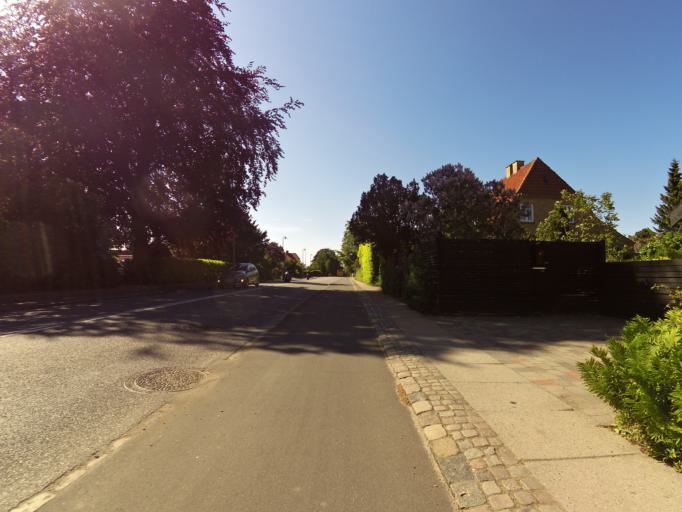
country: DK
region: Capital Region
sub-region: Gladsaxe Municipality
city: Buddinge
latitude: 55.7666
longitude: 12.4860
